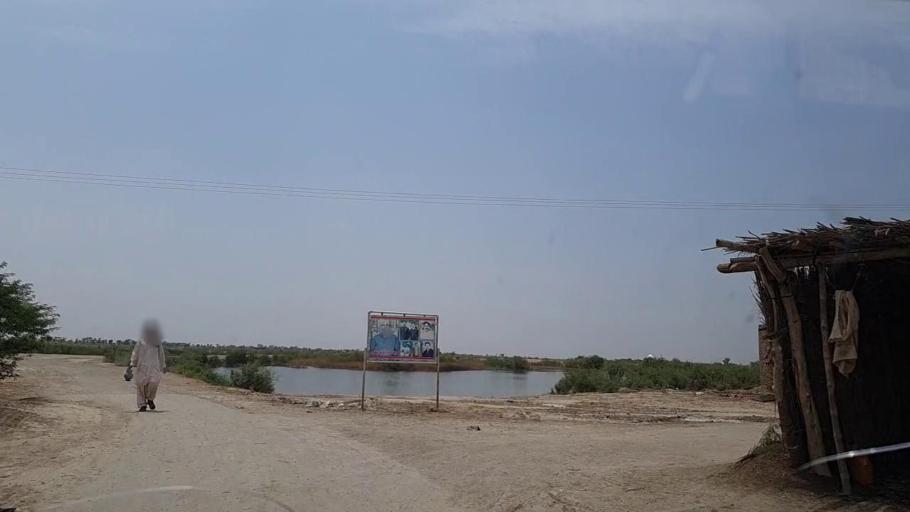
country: PK
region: Sindh
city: Phulji
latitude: 26.8821
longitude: 67.6787
